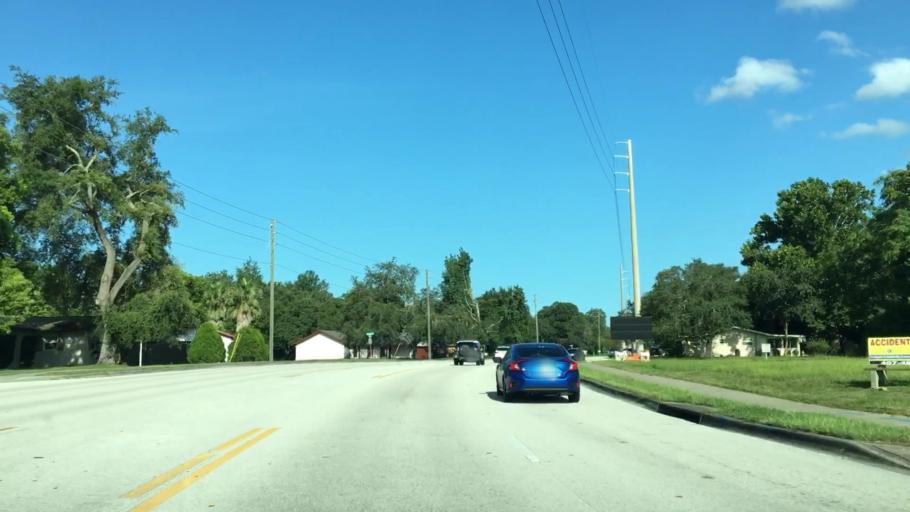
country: US
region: Florida
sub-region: Volusia County
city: Deltona
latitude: 28.9089
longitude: -81.2520
